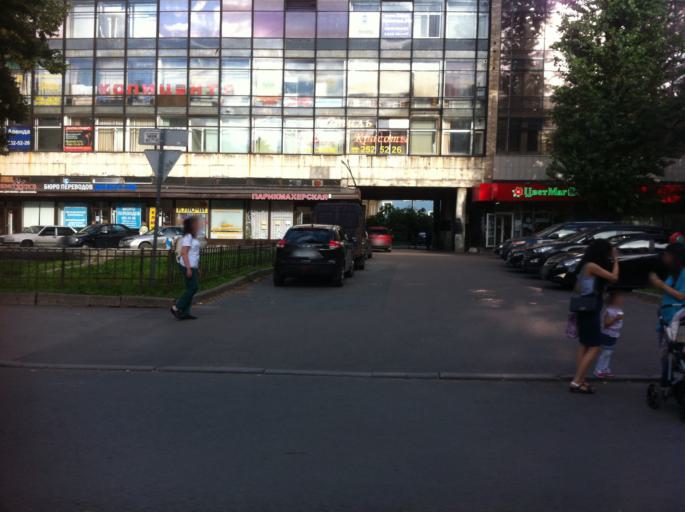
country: RU
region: St.-Petersburg
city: Admiralteisky
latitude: 59.9032
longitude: 30.2739
